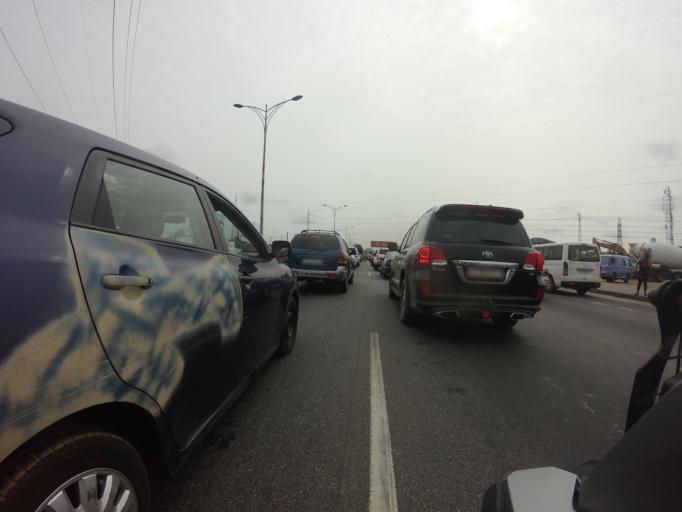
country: GH
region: Greater Accra
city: Dome
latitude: 5.6174
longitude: -0.1955
